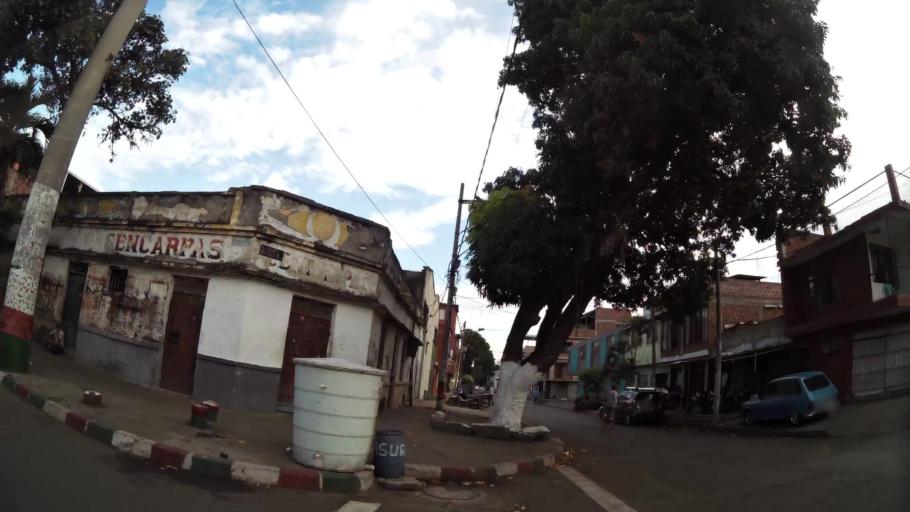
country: CO
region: Valle del Cauca
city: Cali
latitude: 3.4602
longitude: -76.5123
